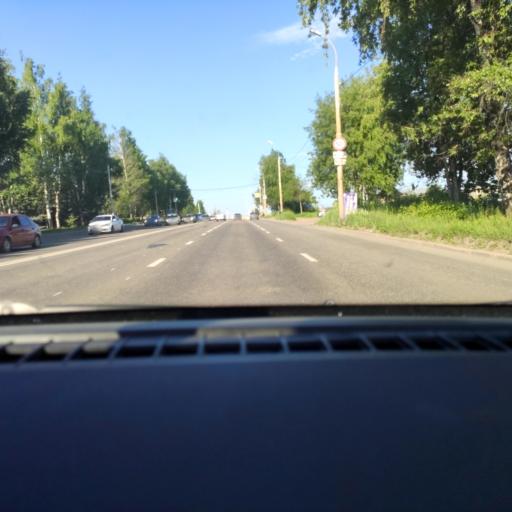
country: RU
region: Udmurtiya
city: Khokhryaki
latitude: 56.9017
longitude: 53.3225
